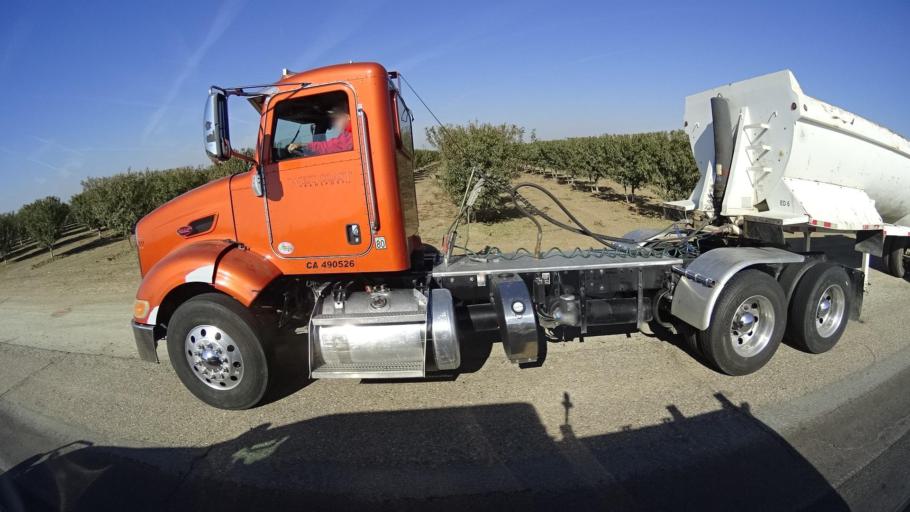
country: US
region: California
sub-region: Kern County
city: McFarland
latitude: 35.6455
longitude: -119.2237
